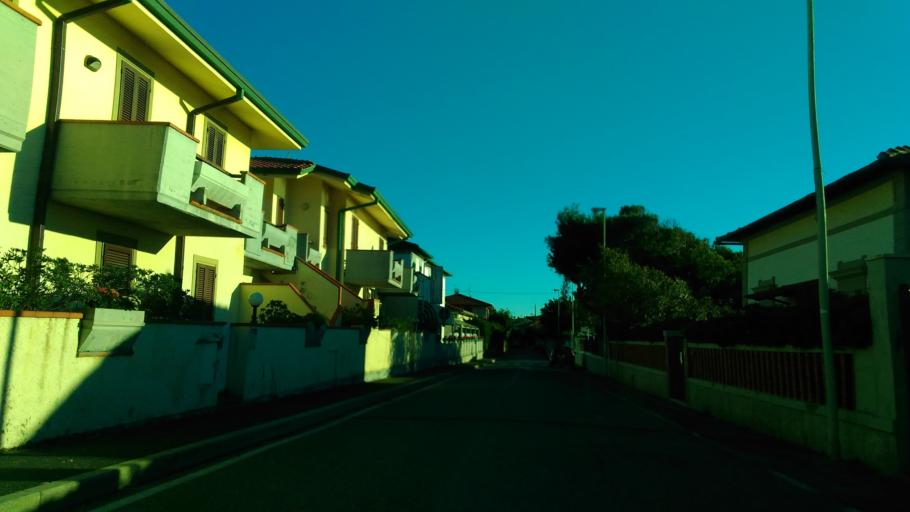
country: IT
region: Tuscany
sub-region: Provincia di Livorno
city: Quercianella
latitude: 43.4536
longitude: 10.3734
